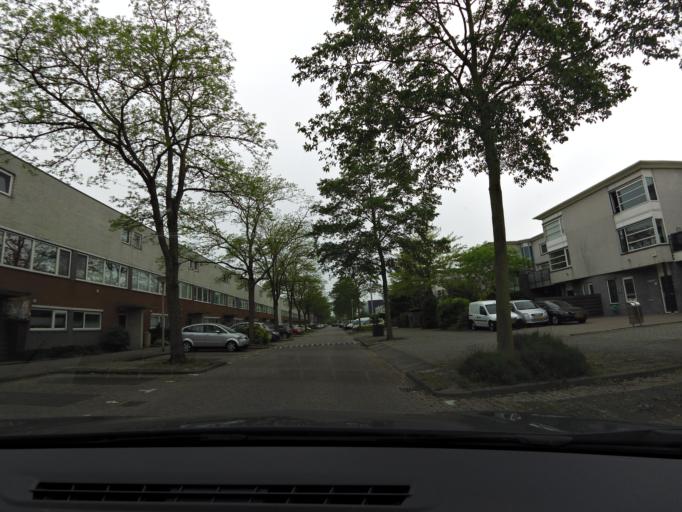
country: NL
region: South Holland
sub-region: Gemeente Delft
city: Delft
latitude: 51.9841
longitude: 4.3402
